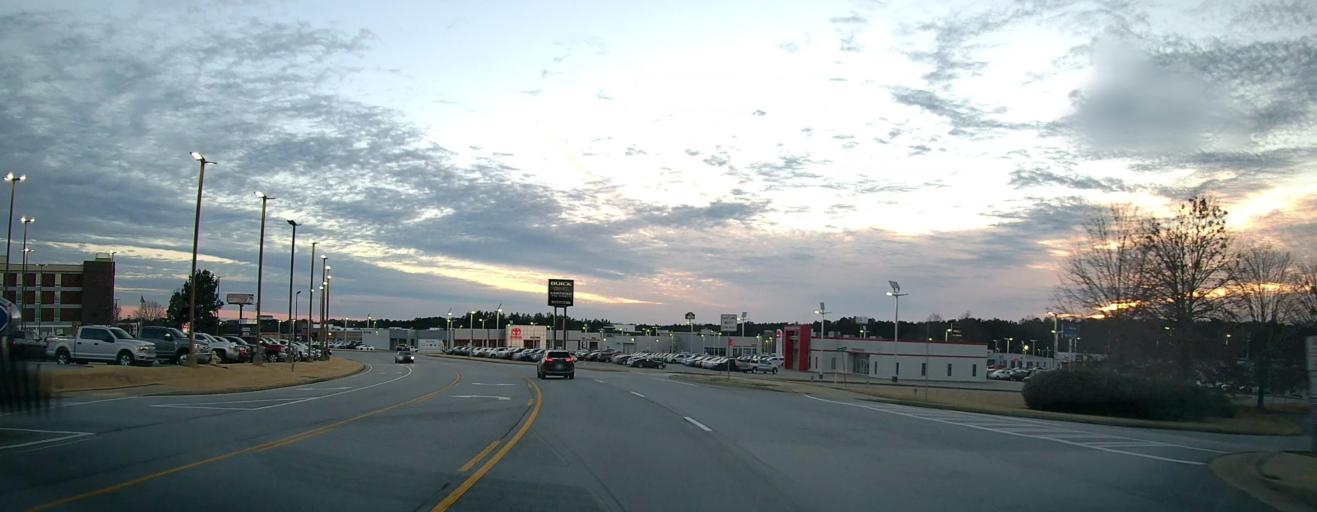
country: US
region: Alabama
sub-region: Russell County
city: Phenix City
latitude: 32.5388
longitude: -84.9686
